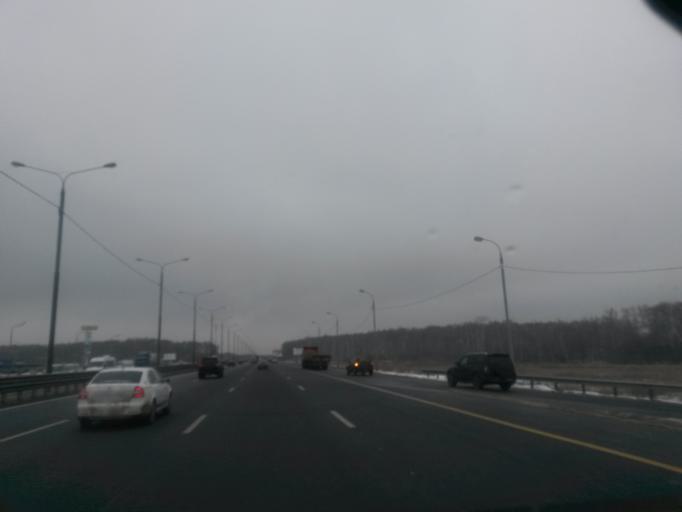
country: RU
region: Moskovskaya
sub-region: Podol'skiy Rayon
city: Podol'sk
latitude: 55.3896
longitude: 37.6052
